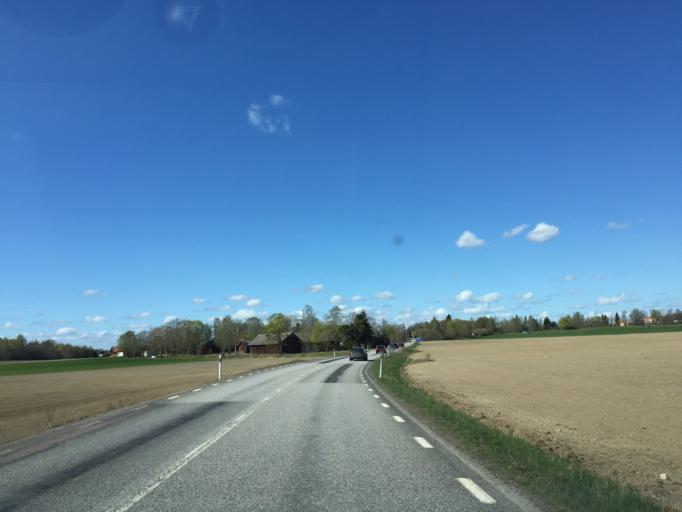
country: SE
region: OErebro
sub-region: Hallsbergs Kommun
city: Skollersta
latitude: 59.1238
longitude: 15.3298
